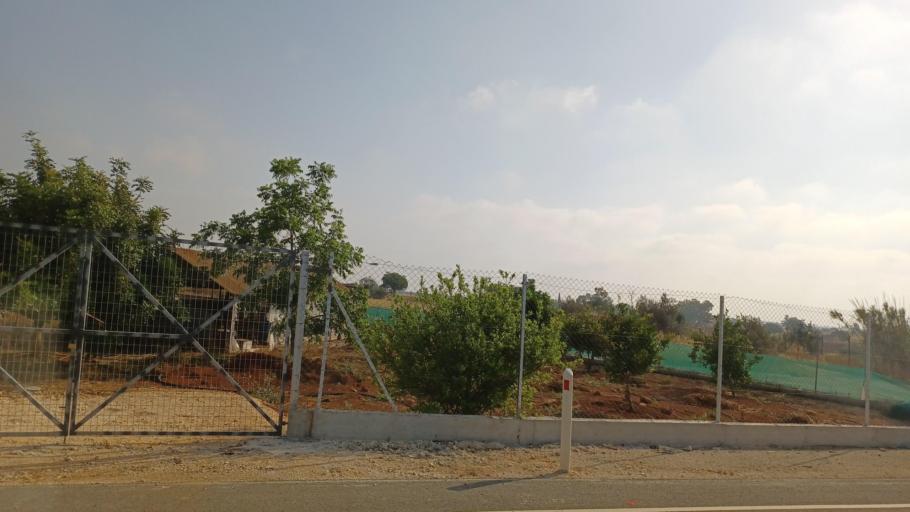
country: CY
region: Ammochostos
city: Avgorou
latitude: 35.0487
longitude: 33.8215
